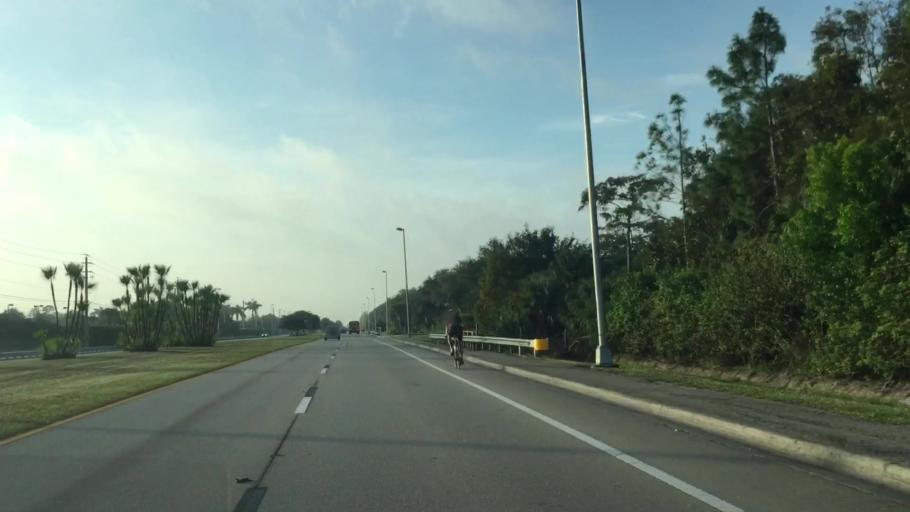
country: US
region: Florida
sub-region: Lee County
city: Estero
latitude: 26.4469
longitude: -81.7889
